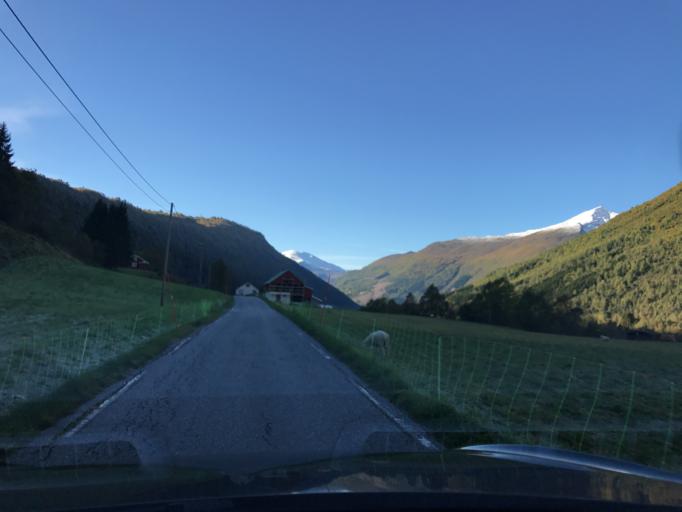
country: NO
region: More og Romsdal
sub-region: Norddal
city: Valldal
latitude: 62.3267
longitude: 7.3354
